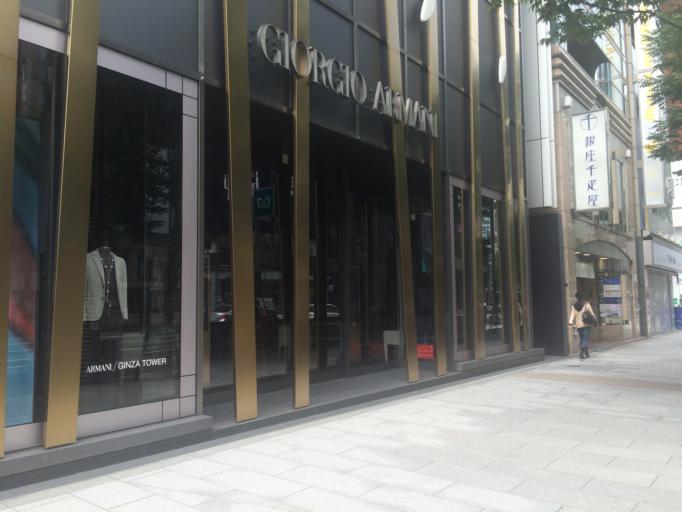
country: JP
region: Tokyo
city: Tokyo
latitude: 35.6718
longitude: 139.7642
